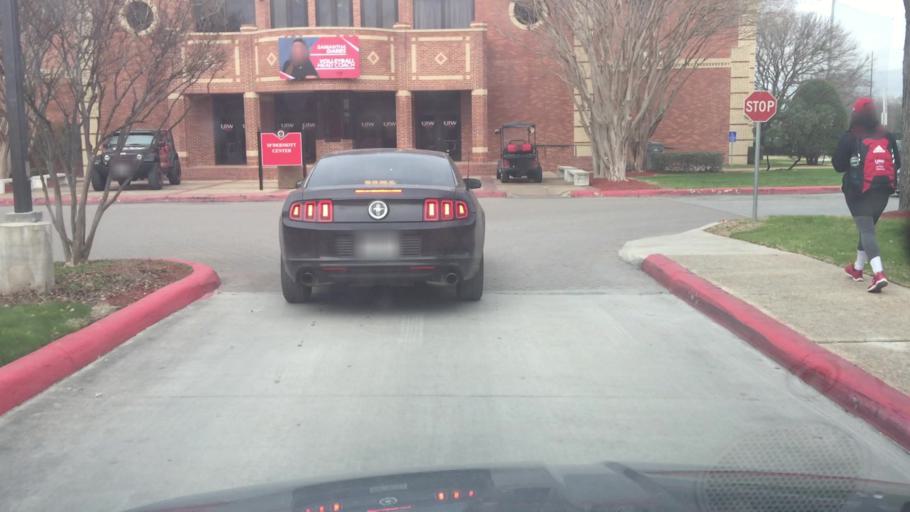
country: US
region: Texas
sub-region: Bexar County
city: Alamo Heights
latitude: 29.4678
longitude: -98.4687
